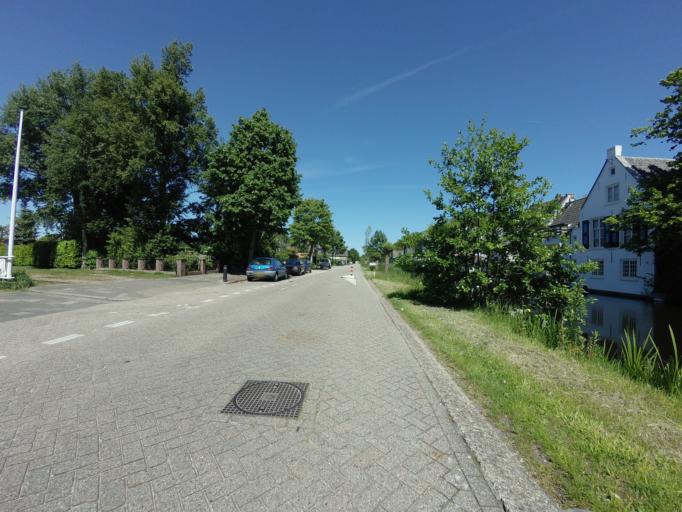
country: NL
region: North Holland
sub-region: Gemeente Wijdemeren
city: Kortenhoef
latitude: 52.2441
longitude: 5.1209
